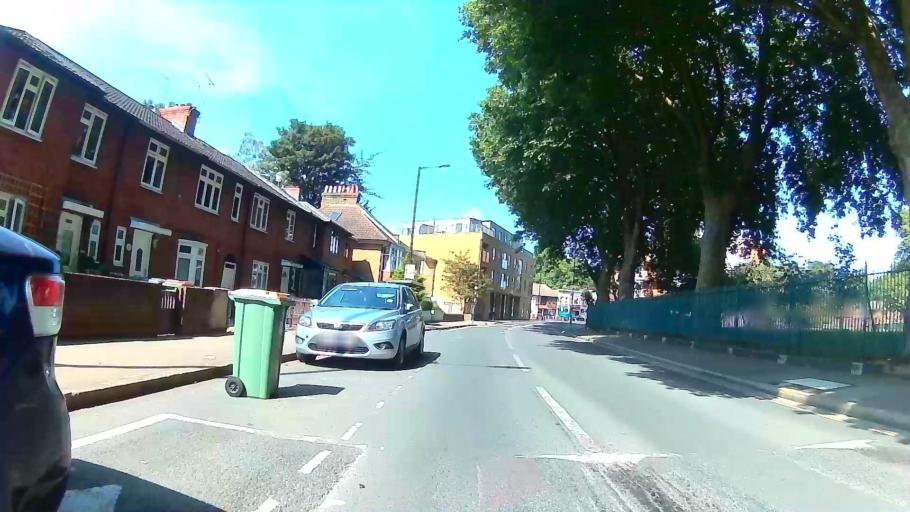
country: GB
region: England
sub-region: Greater London
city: Poplar
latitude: 51.5243
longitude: 0.0128
